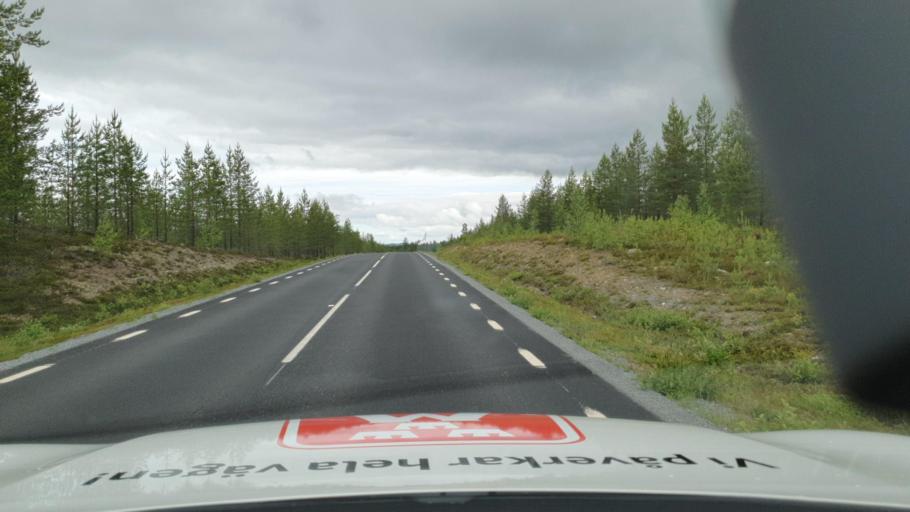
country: SE
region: Vaesterbotten
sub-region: Dorotea Kommun
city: Dorotea
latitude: 64.1918
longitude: 16.5918
